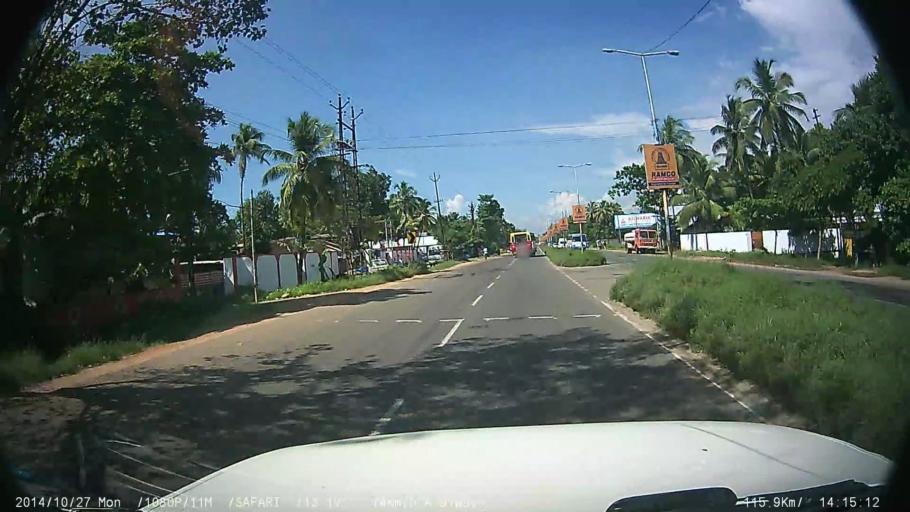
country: IN
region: Kerala
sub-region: Alappuzha
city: Kutiatodu
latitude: 9.8302
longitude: 76.3096
